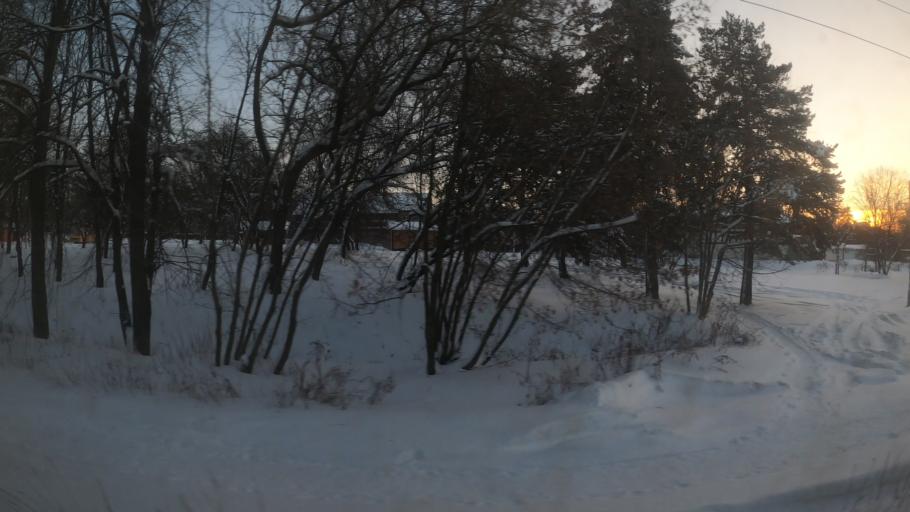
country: RU
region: Moskovskaya
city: Dedenevo
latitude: 56.2419
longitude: 37.5124
